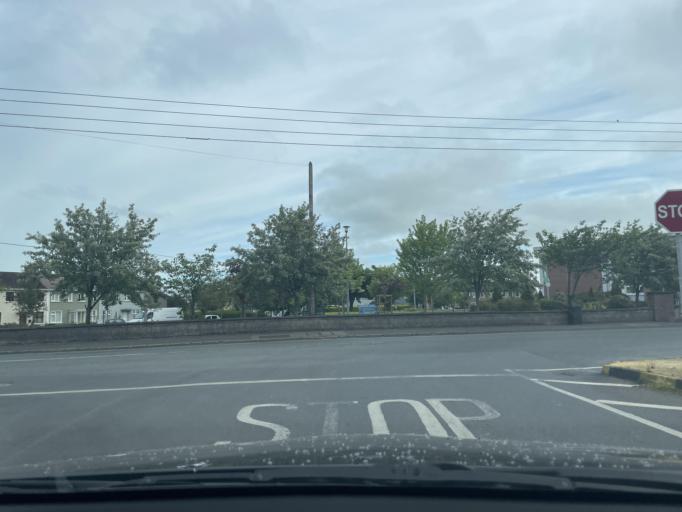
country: IE
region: Leinster
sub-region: County Carlow
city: Bagenalstown
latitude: 52.7016
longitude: -6.9511
